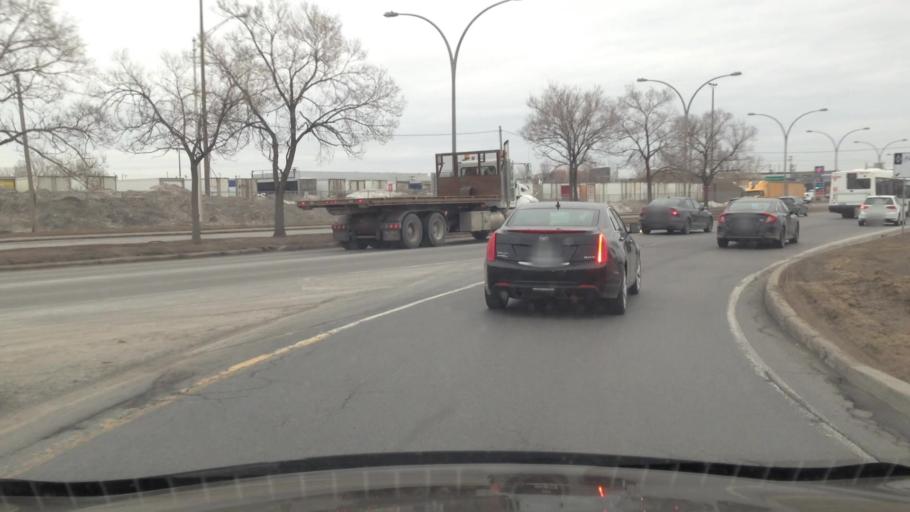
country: CA
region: Quebec
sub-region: Laval
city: Laval
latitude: 45.5834
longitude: -73.7346
